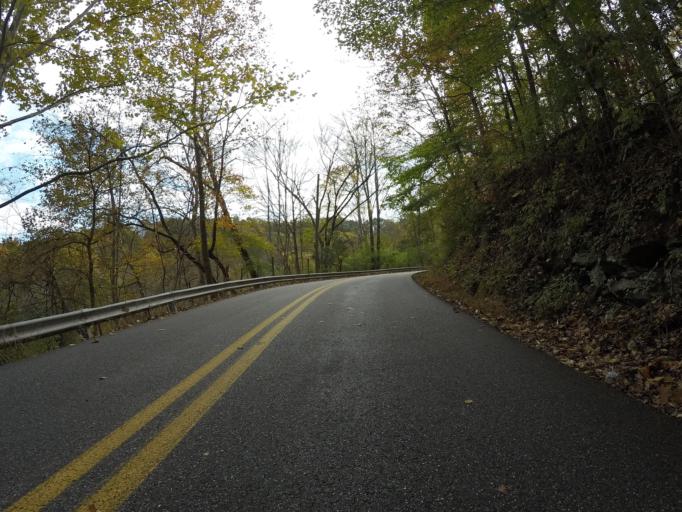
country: US
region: West Virginia
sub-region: Wayne County
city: Lavalette
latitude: 38.3676
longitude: -82.4188
